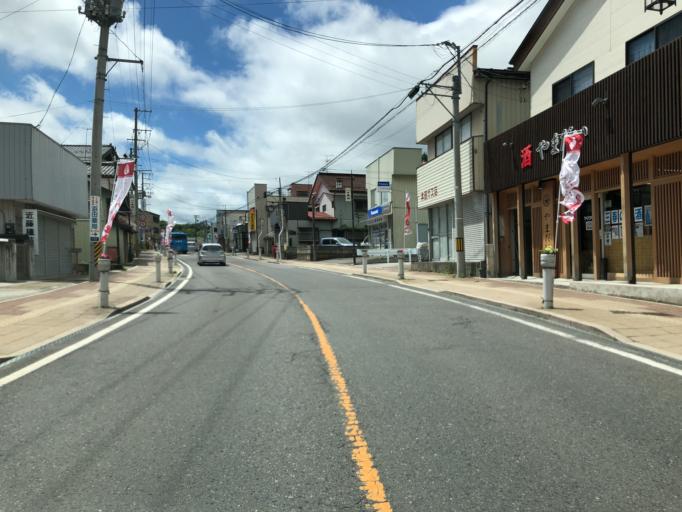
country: JP
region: Fukushima
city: Miharu
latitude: 37.4444
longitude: 140.4875
